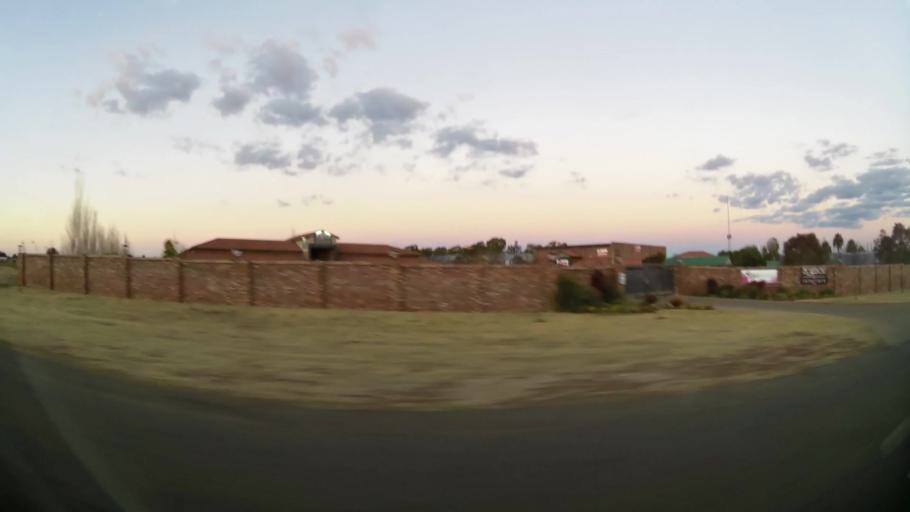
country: ZA
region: North-West
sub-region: Dr Kenneth Kaunda District Municipality
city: Potchefstroom
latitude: -26.7068
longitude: 27.1262
